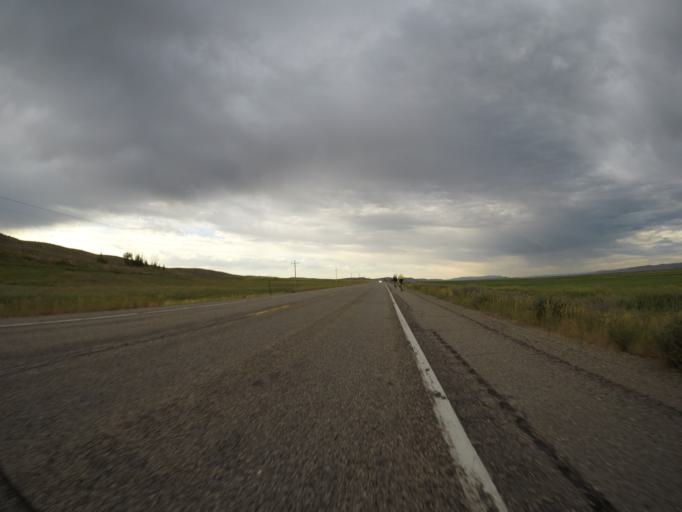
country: US
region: Utah
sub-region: Rich County
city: Randolph
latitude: 41.9630
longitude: -110.9480
